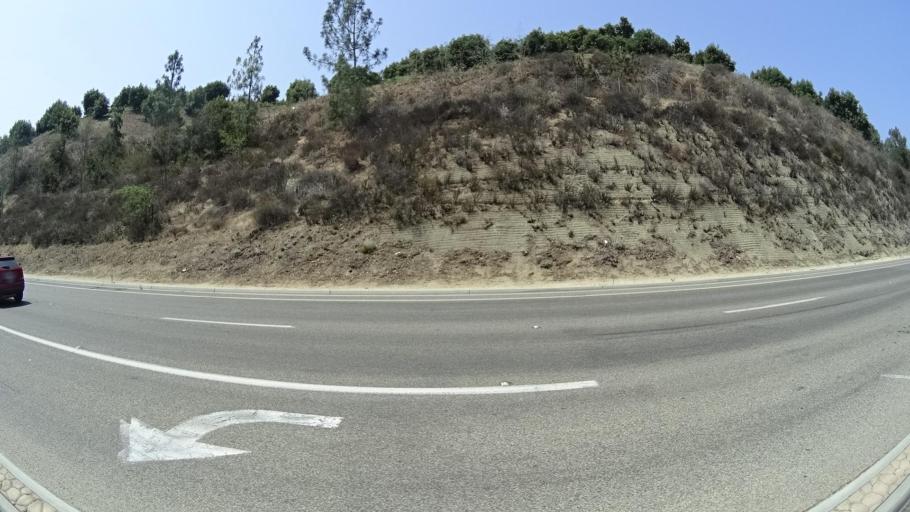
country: US
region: California
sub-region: San Diego County
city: Fallbrook
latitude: 33.3523
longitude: -117.2457
